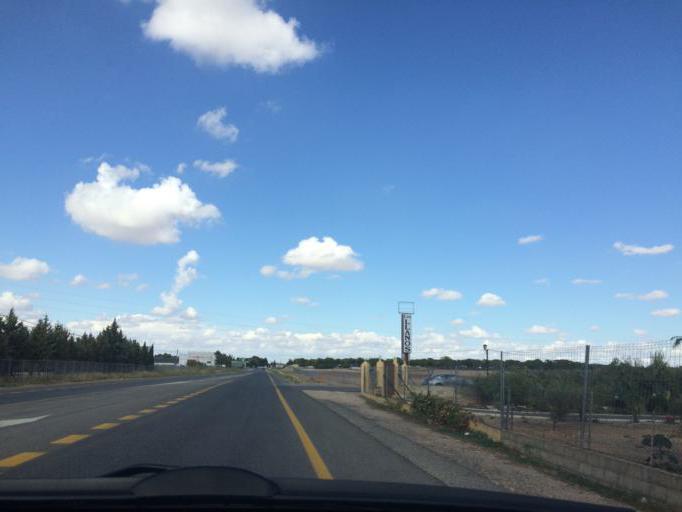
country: ES
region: Castille-La Mancha
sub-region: Provincia de Albacete
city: Albacete
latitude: 38.9591
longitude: -1.8778
